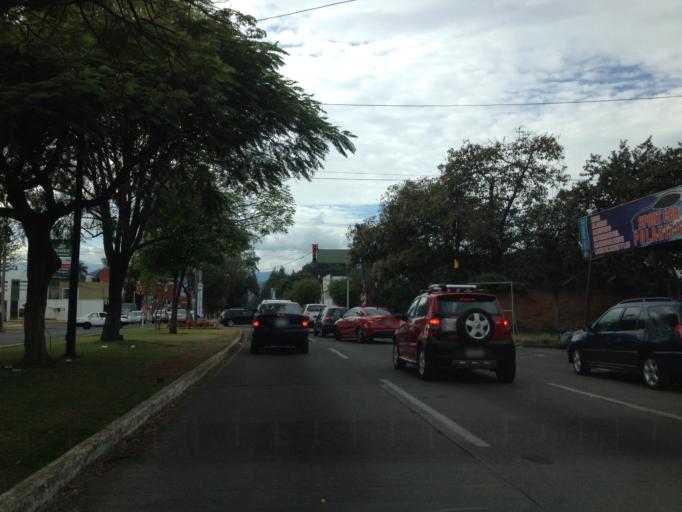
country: MX
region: Michoacan
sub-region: Uruapan
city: Uruapan
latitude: 19.4049
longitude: -102.0487
